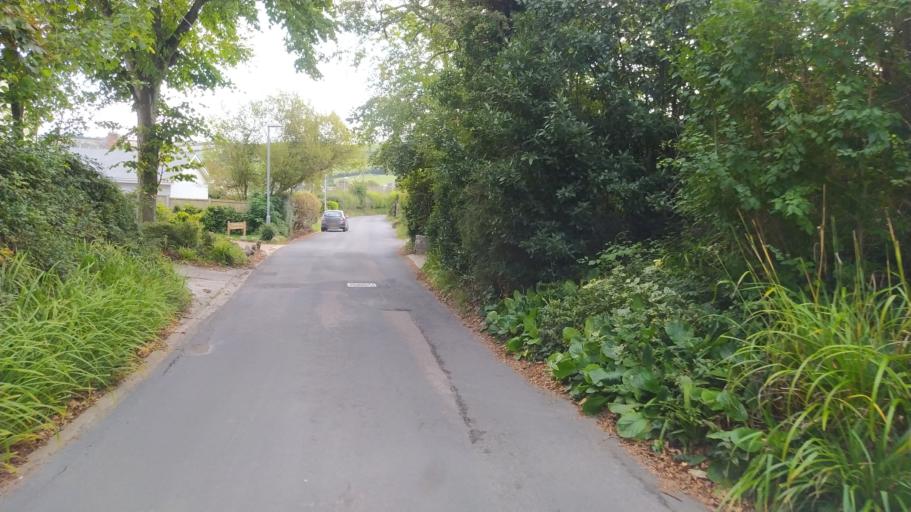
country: GB
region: England
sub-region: Dorset
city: Overcombe
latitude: 50.6556
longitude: -2.4213
